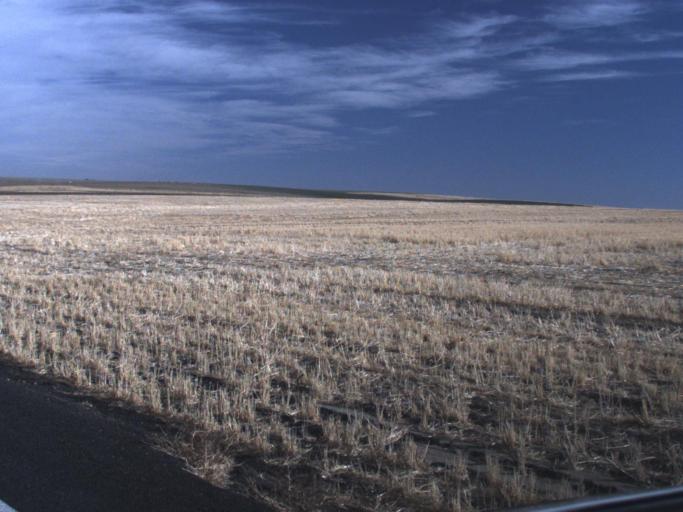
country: US
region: Washington
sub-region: Adams County
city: Ritzville
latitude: 47.2827
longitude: -118.6906
